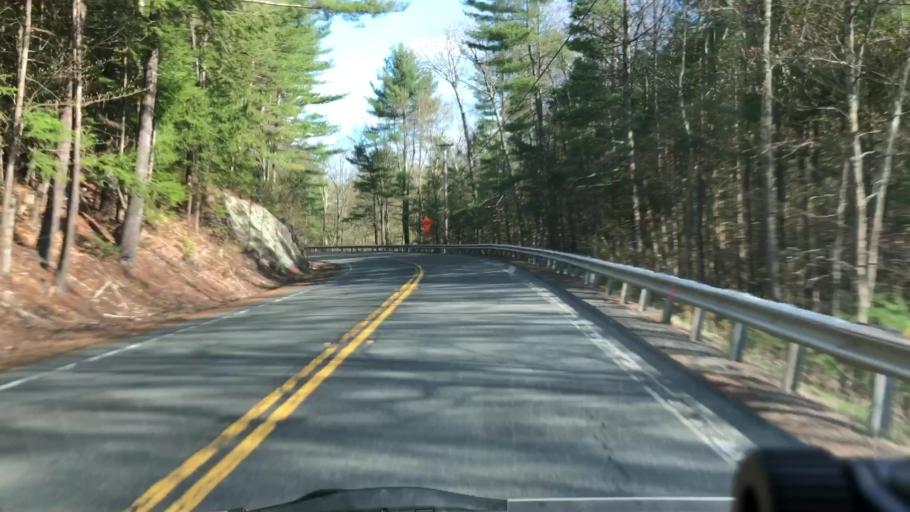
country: US
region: Massachusetts
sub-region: Hampshire County
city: Chesterfield
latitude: 42.3497
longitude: -72.9017
